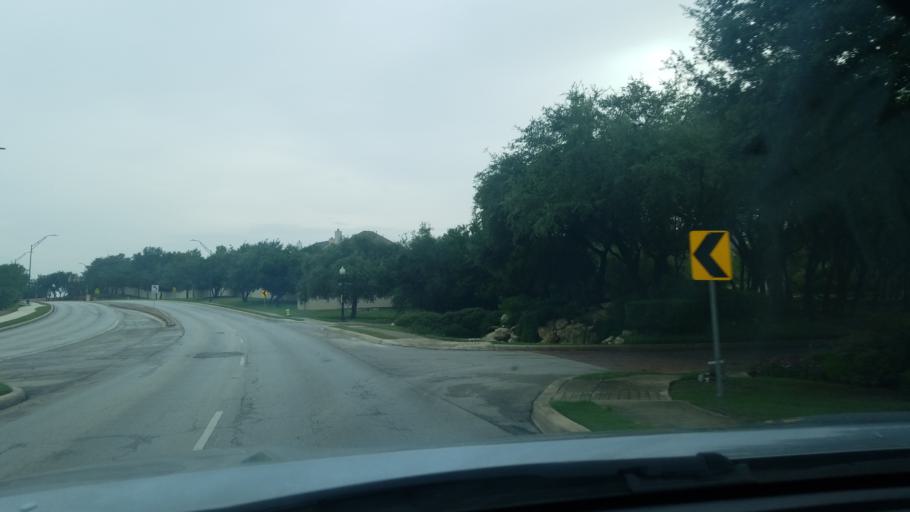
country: US
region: Texas
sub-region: Bexar County
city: Hollywood Park
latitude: 29.6129
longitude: -98.5226
